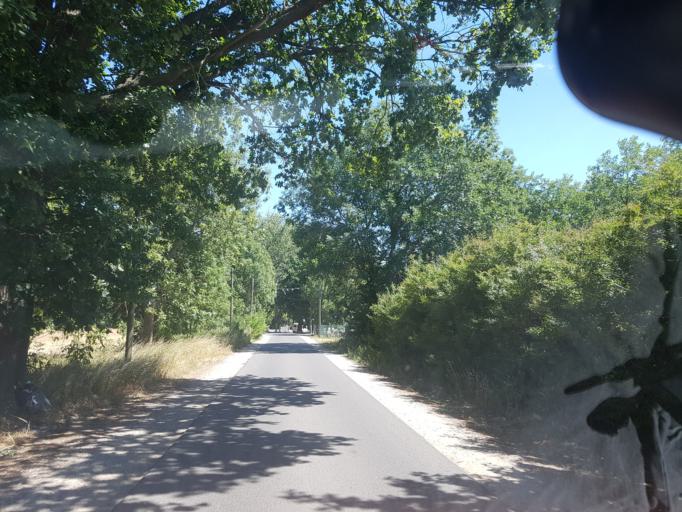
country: DE
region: Brandenburg
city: Teltow
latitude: 52.3889
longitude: 13.2628
